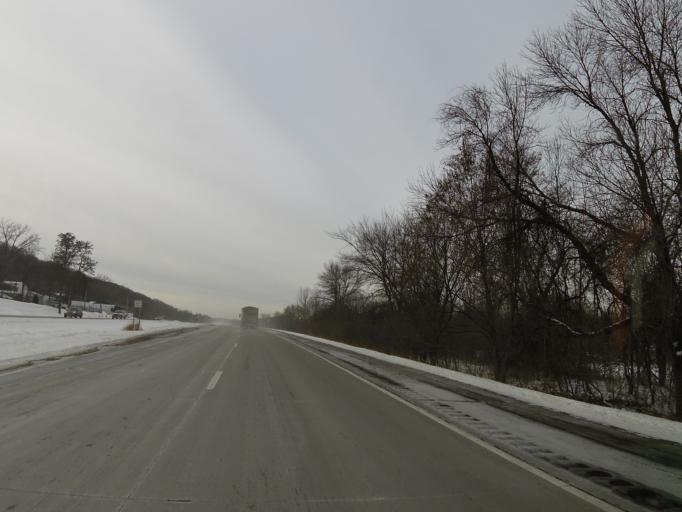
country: US
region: Minnesota
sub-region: Scott County
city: Jordan
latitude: 44.6905
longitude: -93.6067
